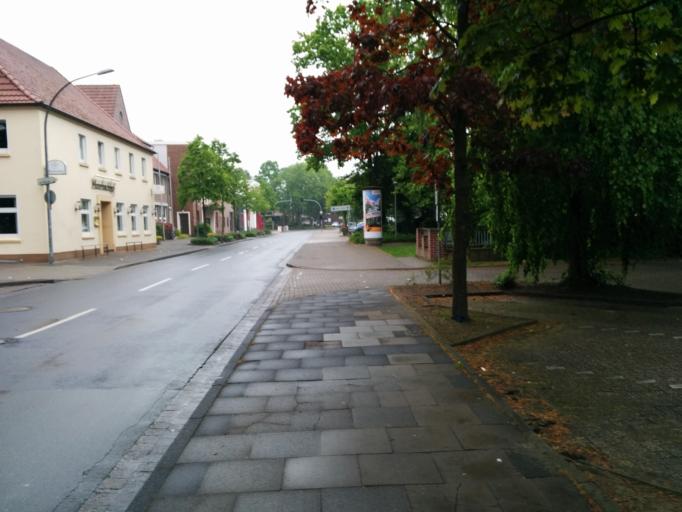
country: DE
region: Lower Saxony
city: Vechta
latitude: 52.7276
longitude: 8.2832
